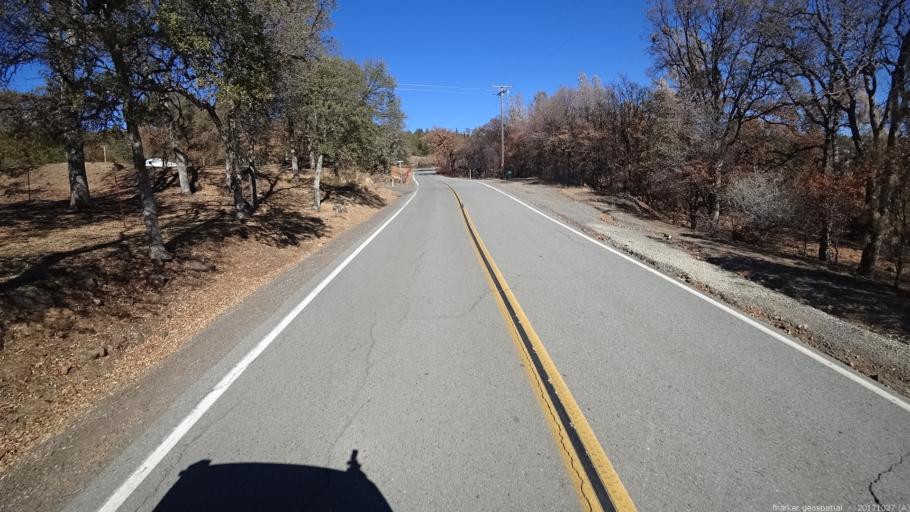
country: US
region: California
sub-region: Shasta County
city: Bella Vista
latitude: 40.7160
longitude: -122.0327
